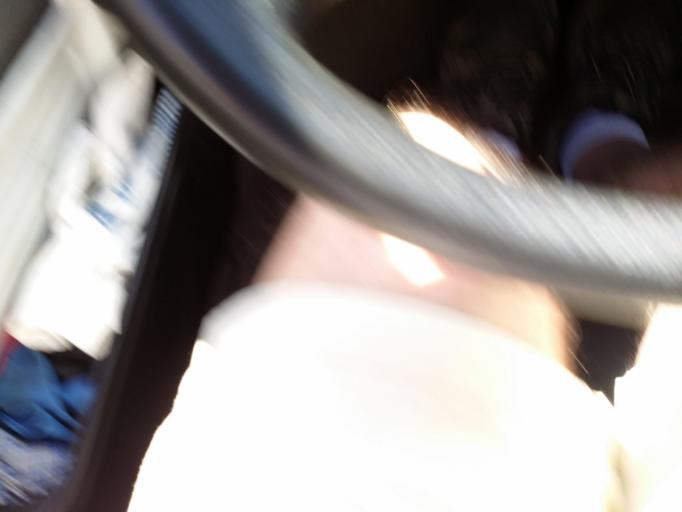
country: IT
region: Liguria
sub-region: Provincia di Genova
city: Genoa
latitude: 44.4047
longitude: 8.9637
